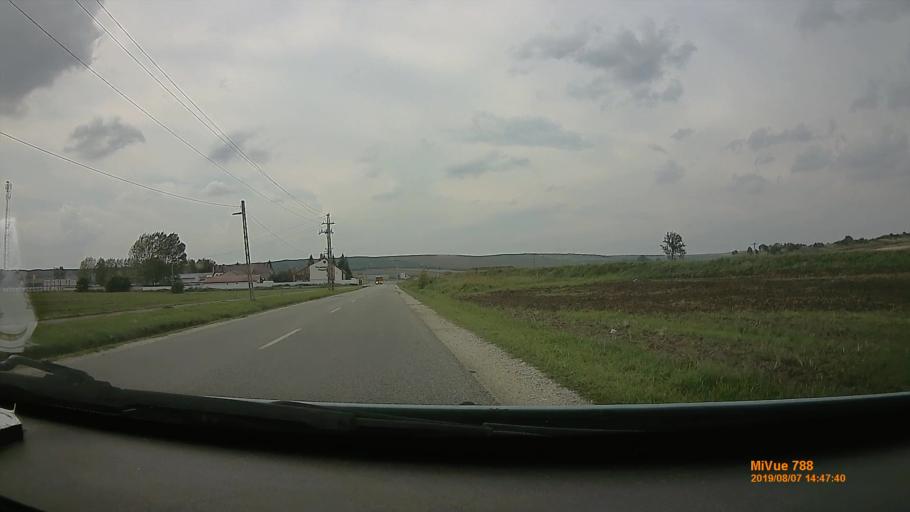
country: HU
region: Borsod-Abauj-Zemplen
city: Halmaj
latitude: 48.2511
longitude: 20.9842
